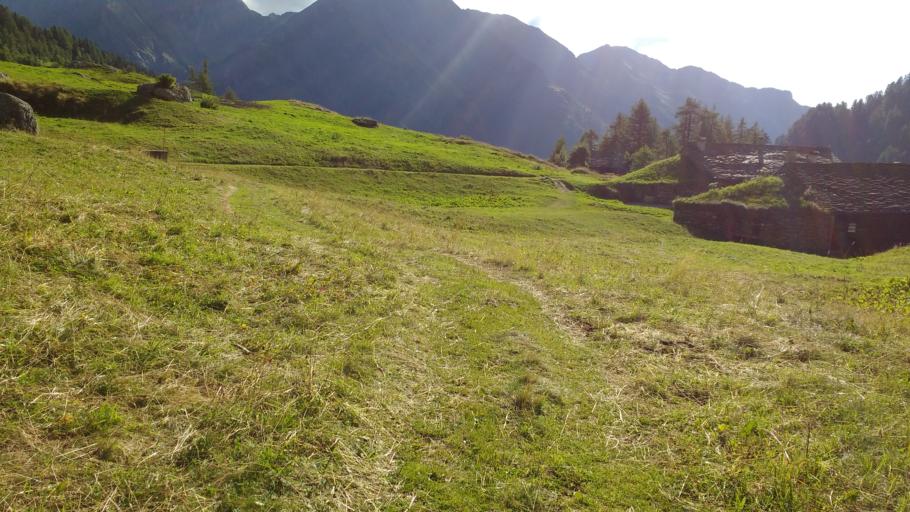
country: IT
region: Piedmont
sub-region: Provincia di Vercelli
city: Alagna Valsesia
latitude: 45.8440
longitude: 7.9144
